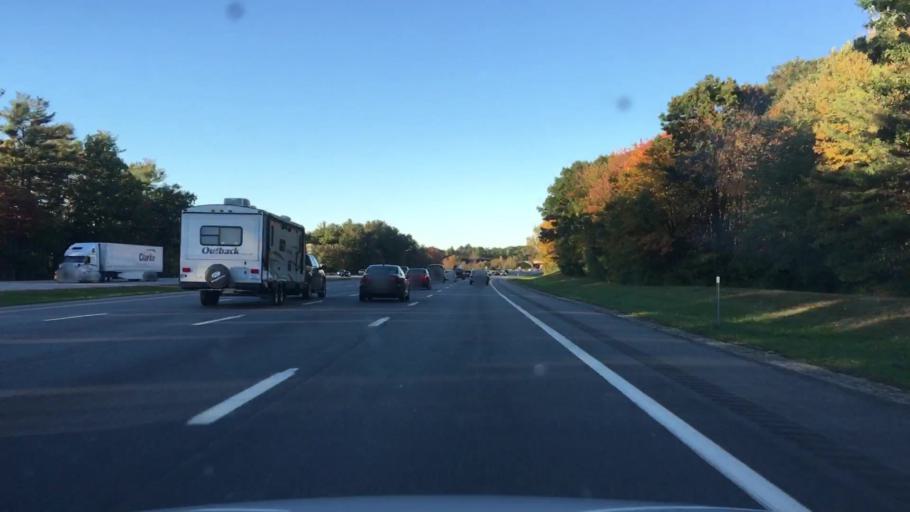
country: US
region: New Hampshire
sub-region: Rockingham County
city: North Hampton
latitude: 42.9862
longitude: -70.8512
